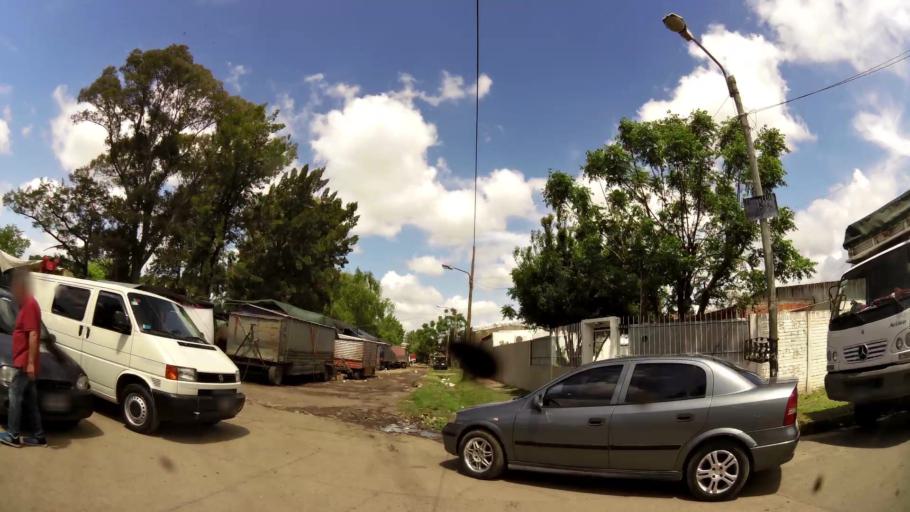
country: AR
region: Buenos Aires
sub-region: Partido de Quilmes
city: Quilmes
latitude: -34.8236
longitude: -58.2272
